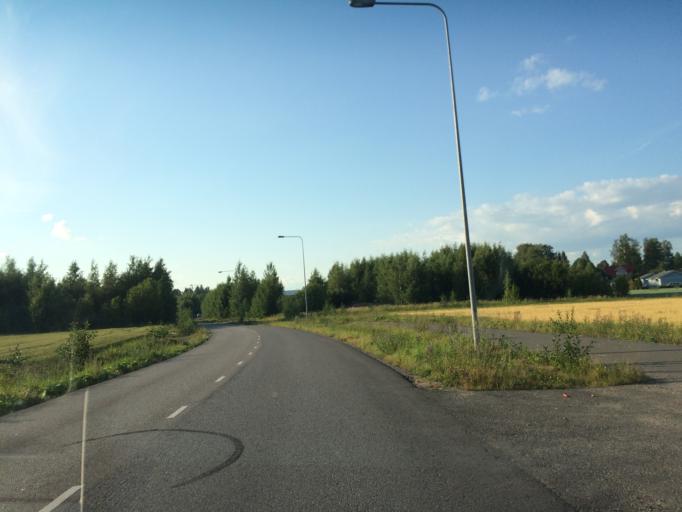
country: FI
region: Haeme
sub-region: Haemeenlinna
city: Parola
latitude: 61.0410
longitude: 24.3813
